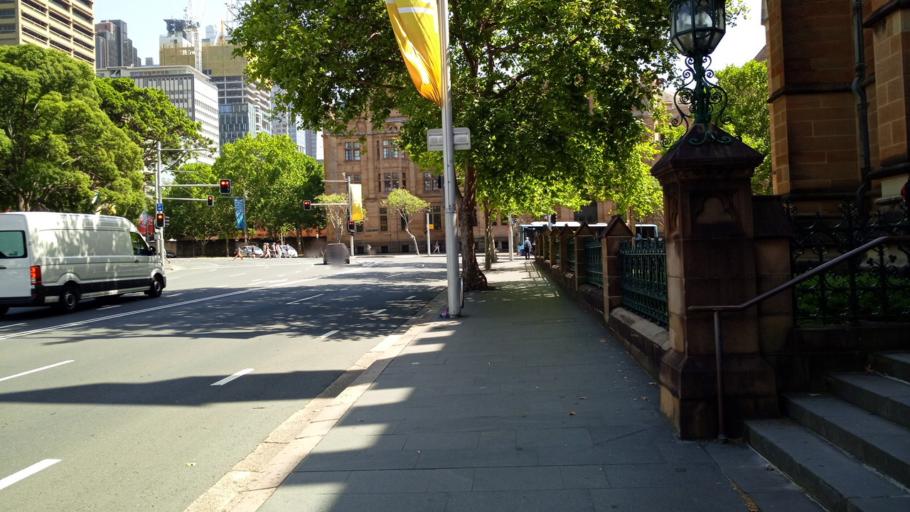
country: AU
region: New South Wales
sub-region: City of Sydney
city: Sydney
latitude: -33.8717
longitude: 151.2122
